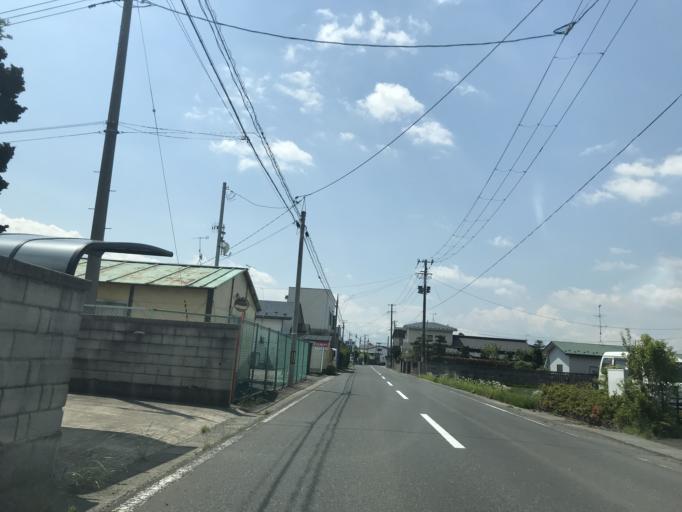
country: JP
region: Miyagi
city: Kogota
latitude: 38.6032
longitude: 141.0223
